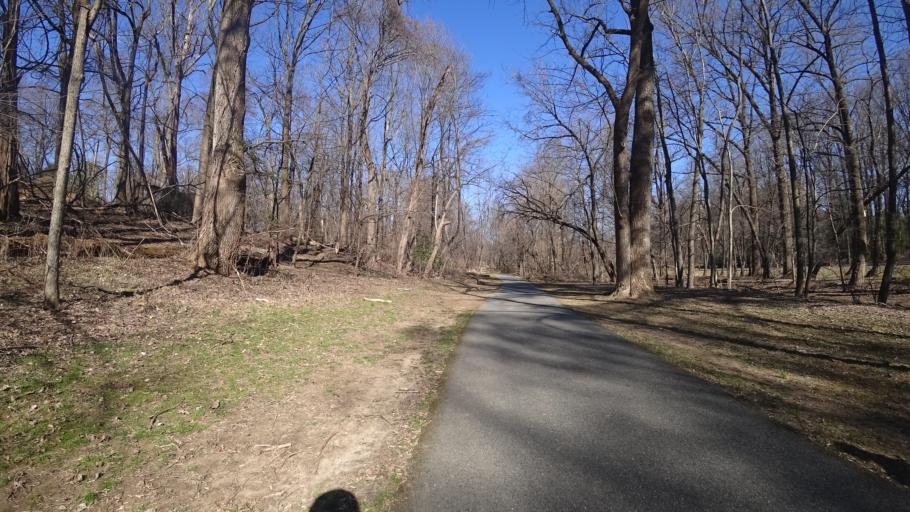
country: US
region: Maryland
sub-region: Montgomery County
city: Kemp Mill
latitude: 39.0344
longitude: -77.0303
